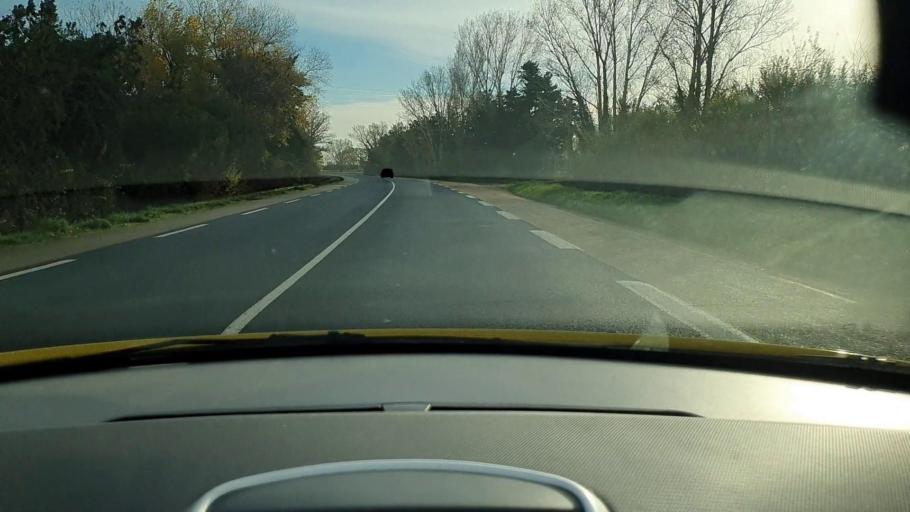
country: FR
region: Languedoc-Roussillon
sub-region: Departement du Gard
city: Fourques
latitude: 43.6998
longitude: 4.5771
